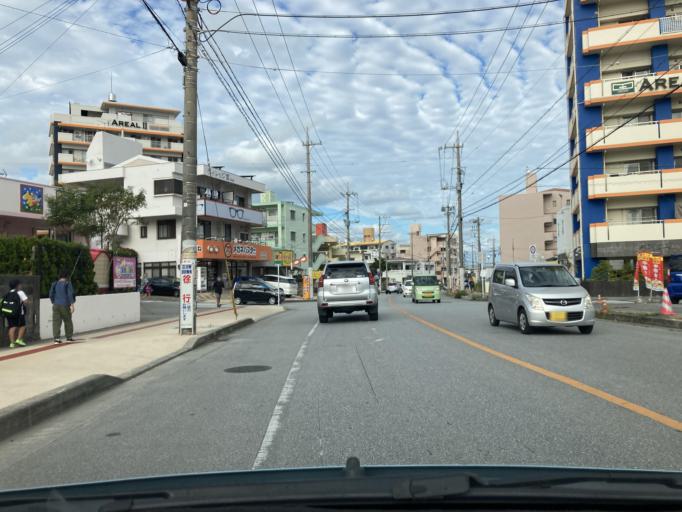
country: JP
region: Okinawa
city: Okinawa
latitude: 26.3411
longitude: 127.8224
